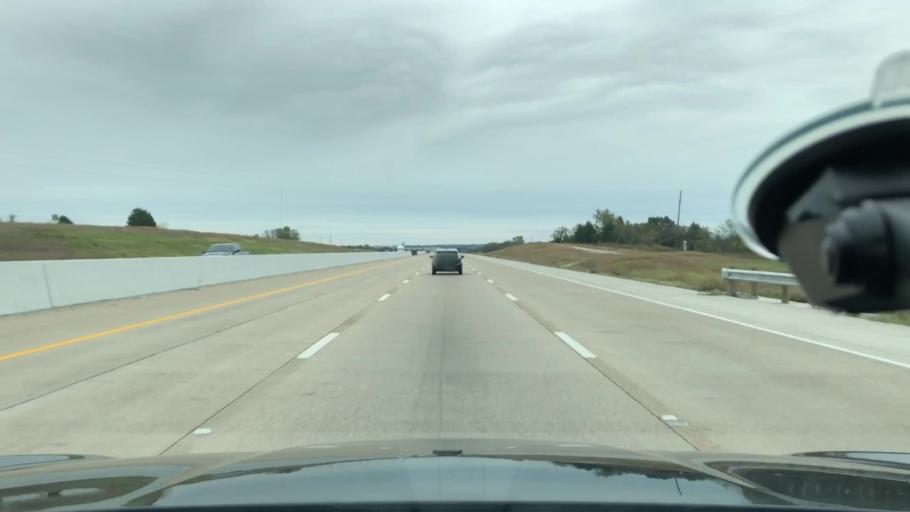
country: US
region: Texas
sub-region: Ellis County
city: Italy
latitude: 32.2116
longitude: -96.8915
